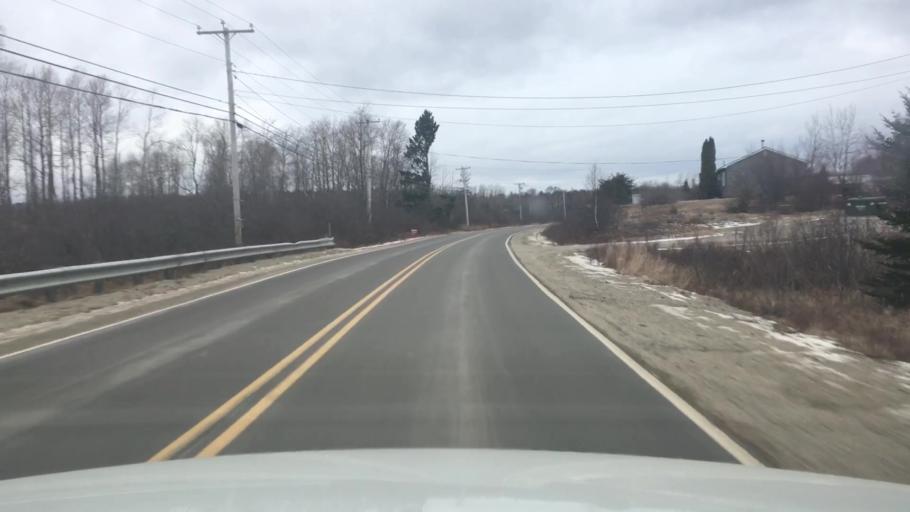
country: US
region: Maine
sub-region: Washington County
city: Jonesport
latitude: 44.5532
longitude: -67.6246
